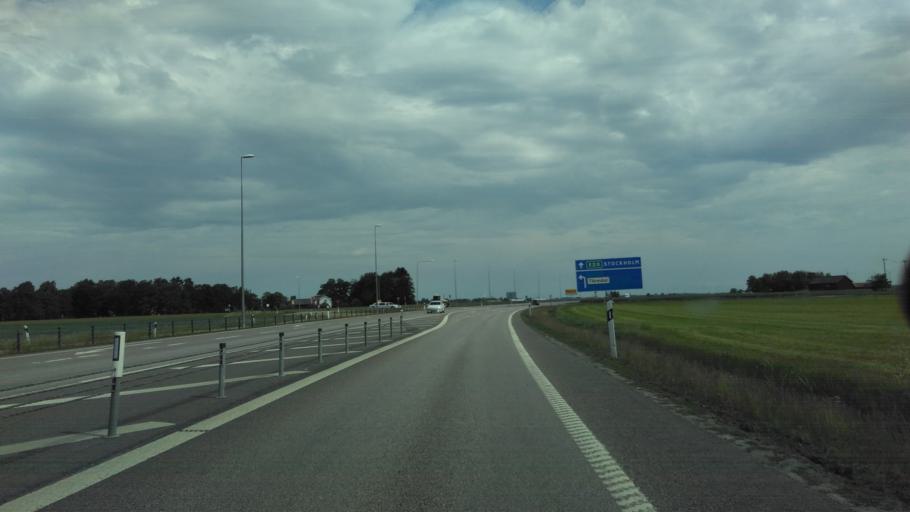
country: SE
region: Vaestra Goetaland
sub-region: Vara Kommun
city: Kvanum
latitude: 58.3074
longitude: 13.0882
